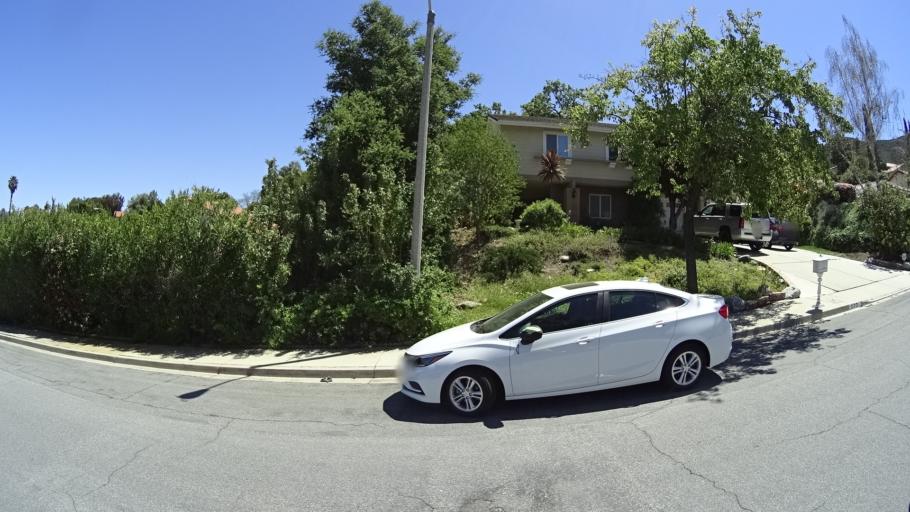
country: US
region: California
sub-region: Ventura County
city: Casa Conejo
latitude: 34.1753
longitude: -118.8995
